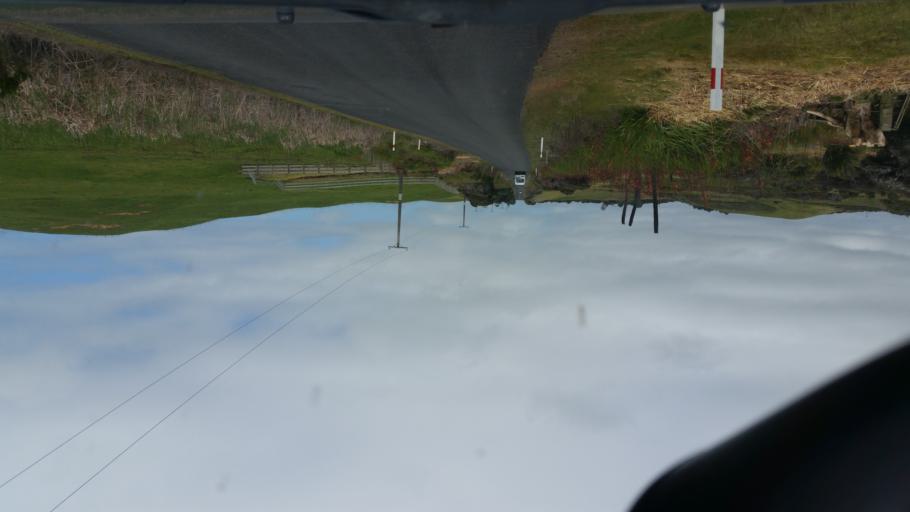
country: NZ
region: Northland
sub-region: Kaipara District
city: Dargaville
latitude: -35.8113
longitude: 173.6377
